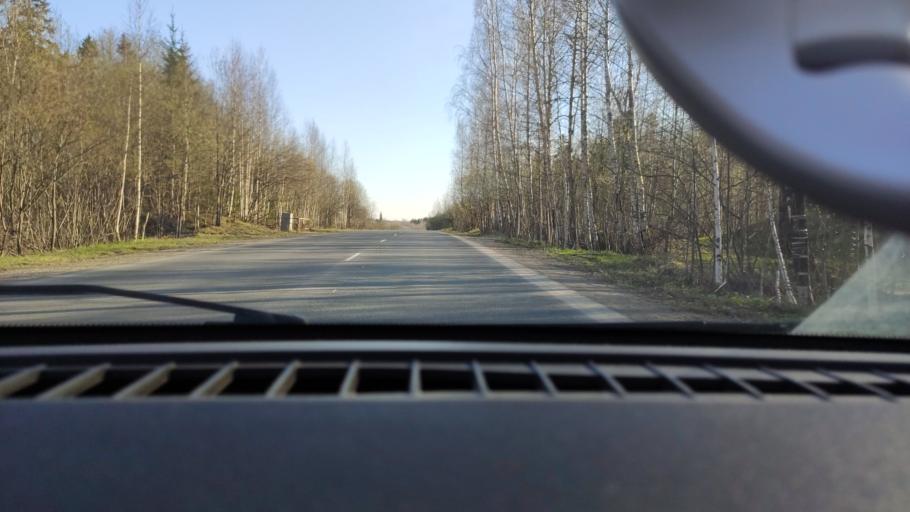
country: RU
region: Perm
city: Polazna
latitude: 58.1197
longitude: 56.4303
